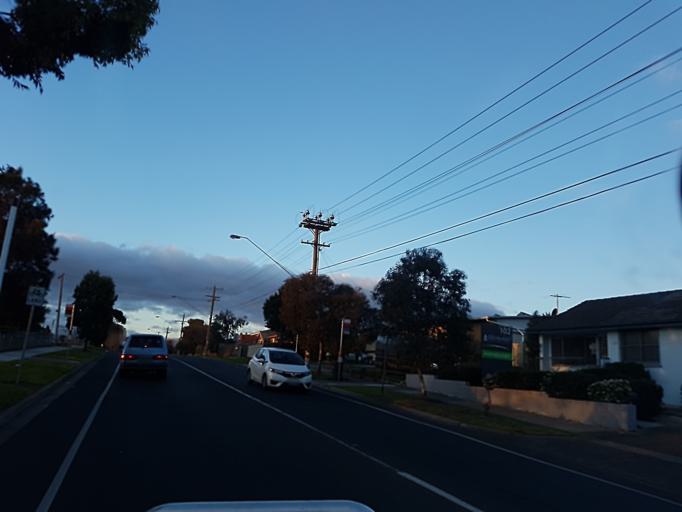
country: AU
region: Victoria
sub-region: Hume
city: Broadmeadows
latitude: -37.6755
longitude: 144.9294
